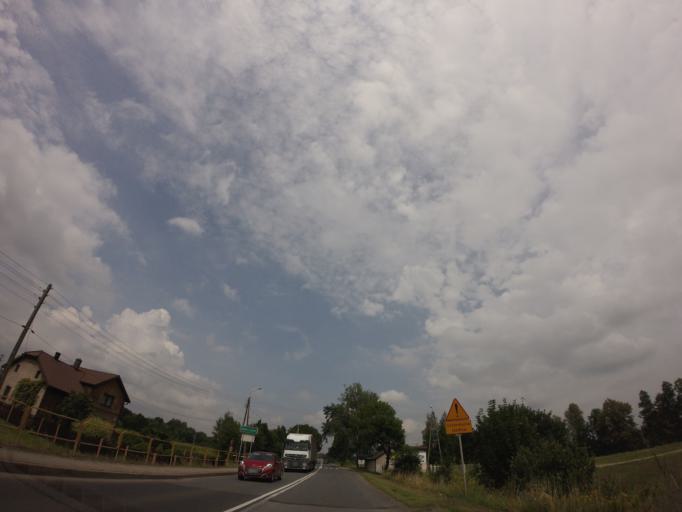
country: PL
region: Silesian Voivodeship
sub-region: Powiat bierunsko-ledzinski
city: Imielin
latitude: 50.1311
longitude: 19.1989
